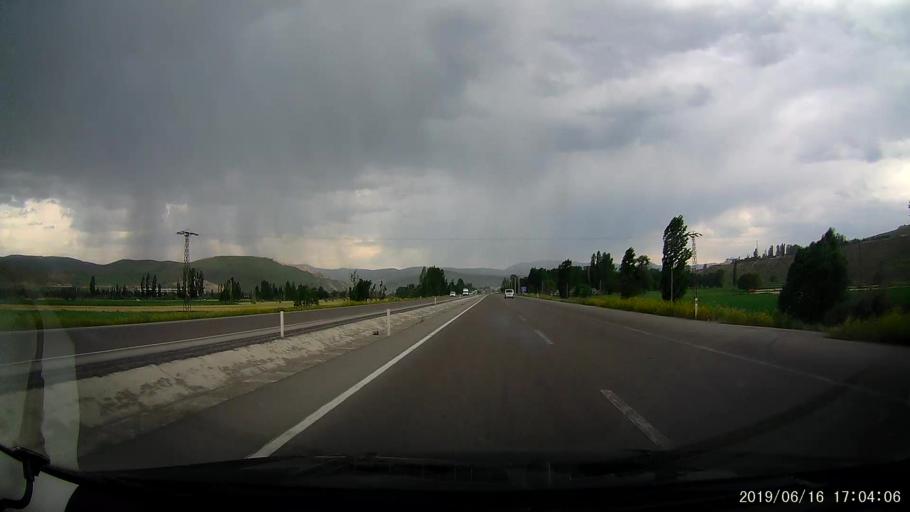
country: TR
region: Erzurum
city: Askale
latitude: 39.9294
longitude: 40.7164
